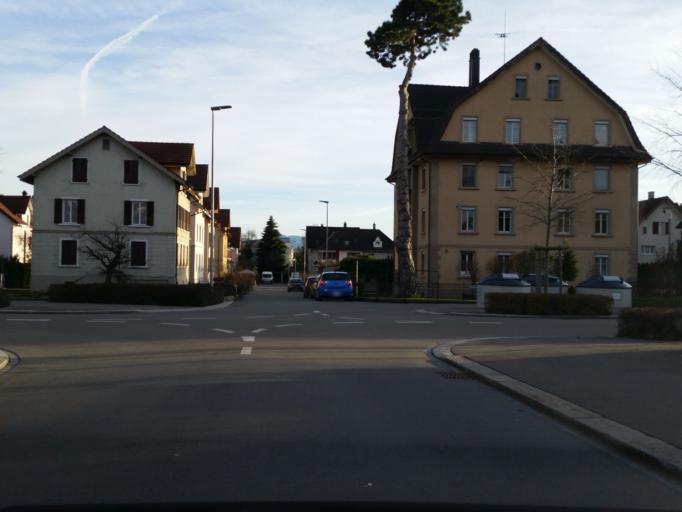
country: CH
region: Thurgau
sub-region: Arbon District
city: Romanshorn
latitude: 47.5627
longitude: 9.3743
